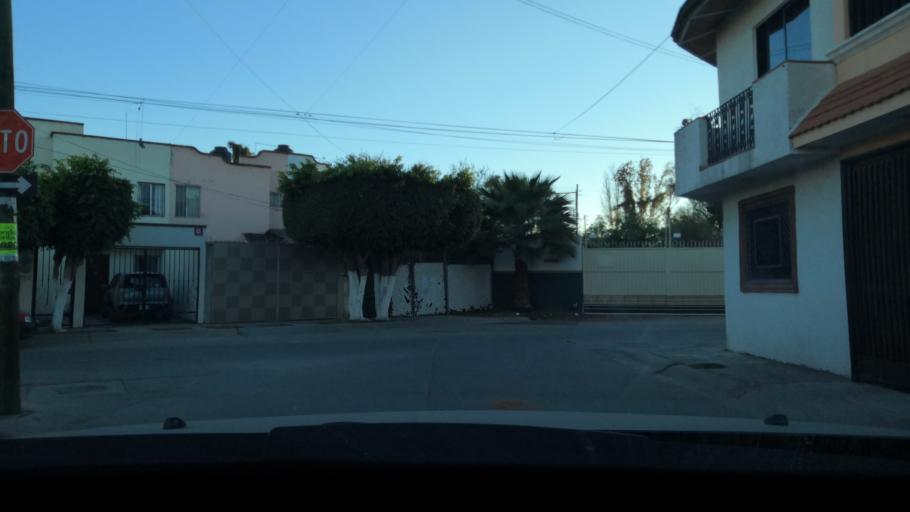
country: MX
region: Guanajuato
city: Leon
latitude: 21.1644
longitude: -101.6591
